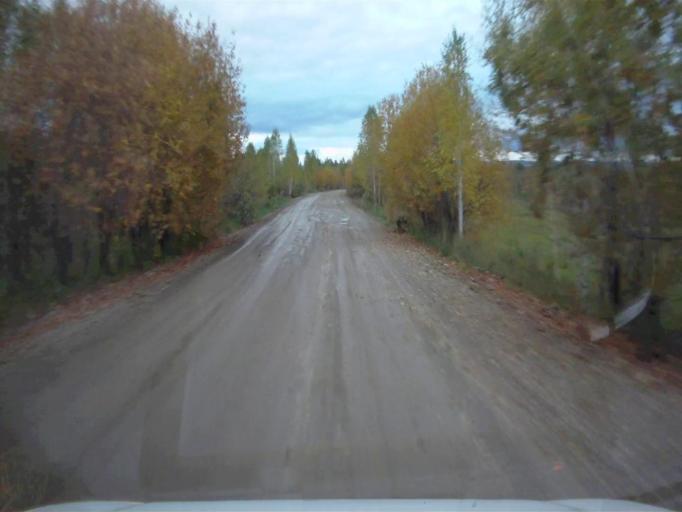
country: RU
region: Sverdlovsk
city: Mikhaylovsk
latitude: 56.2061
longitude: 59.2048
